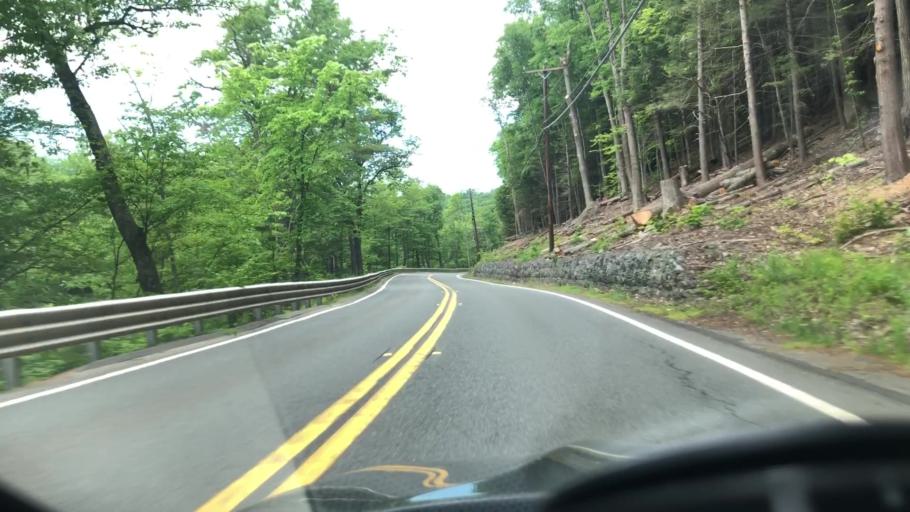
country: US
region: Massachusetts
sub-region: Hampshire County
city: Westhampton
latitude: 42.2559
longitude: -72.8661
